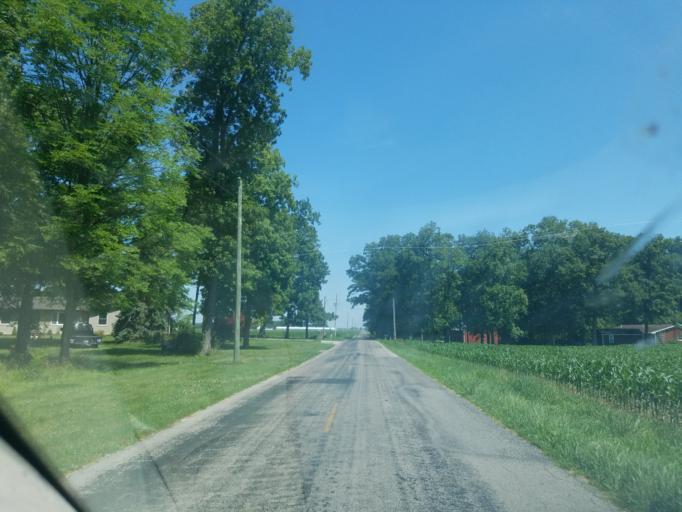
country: US
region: Ohio
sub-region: Mercer County
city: Saint Henry
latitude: 40.4570
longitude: -84.7080
